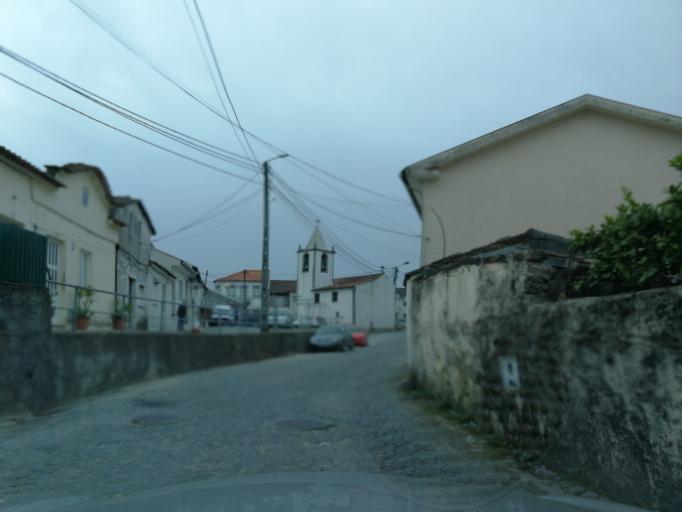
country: PT
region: Braga
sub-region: Braga
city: Braga
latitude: 41.5680
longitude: -8.4388
